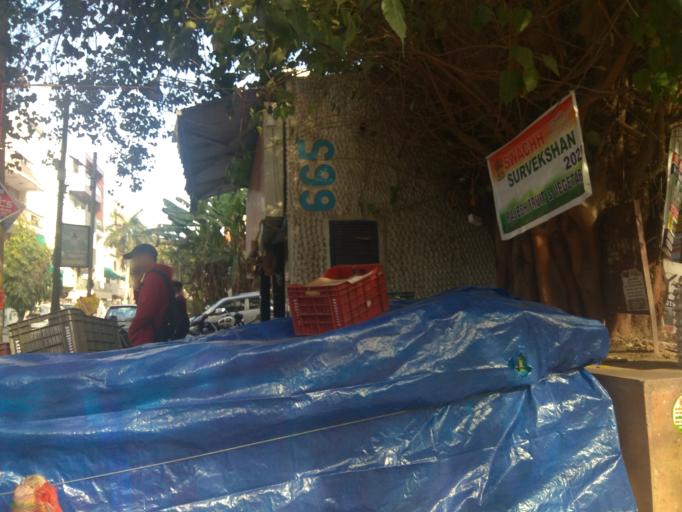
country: IN
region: NCT
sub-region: West Delhi
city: Nangloi Jat
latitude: 28.6283
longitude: 77.0675
